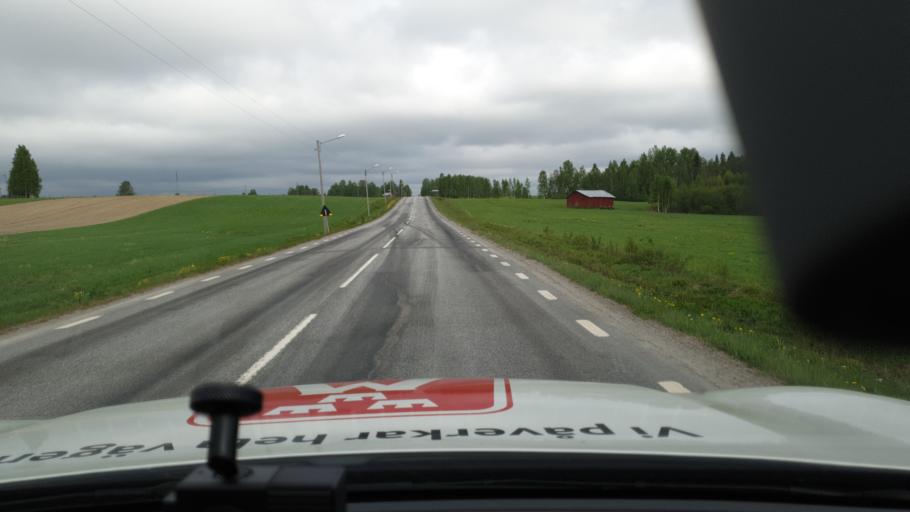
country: SE
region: Vaesterbotten
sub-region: Umea Kommun
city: Roback
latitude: 63.9249
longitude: 20.1856
